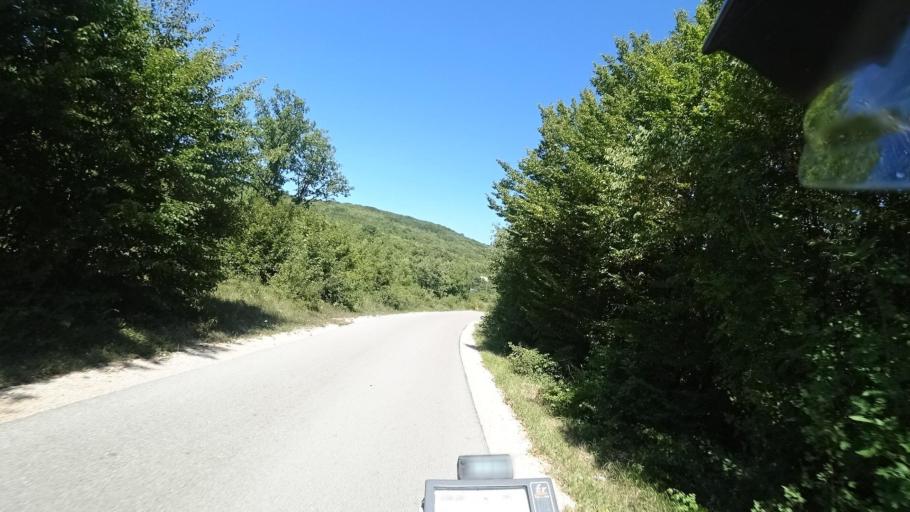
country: HR
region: Licko-Senjska
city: Otocac
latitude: 44.7335
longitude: 15.3498
